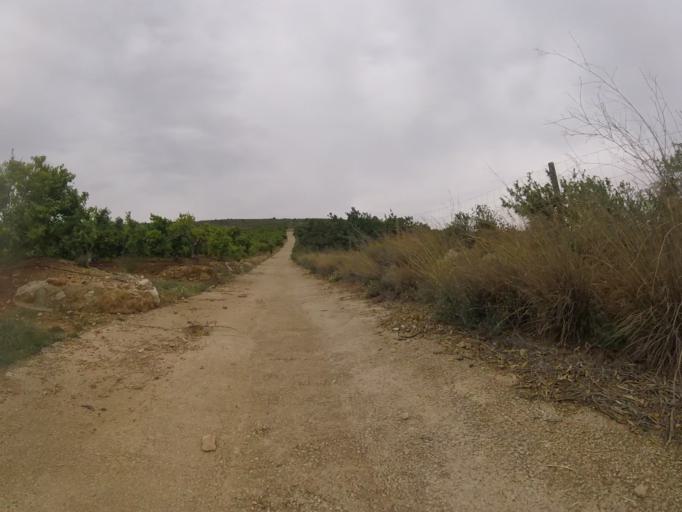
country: ES
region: Valencia
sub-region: Provincia de Castello
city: Alcala de Xivert
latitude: 40.2795
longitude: 0.2524
